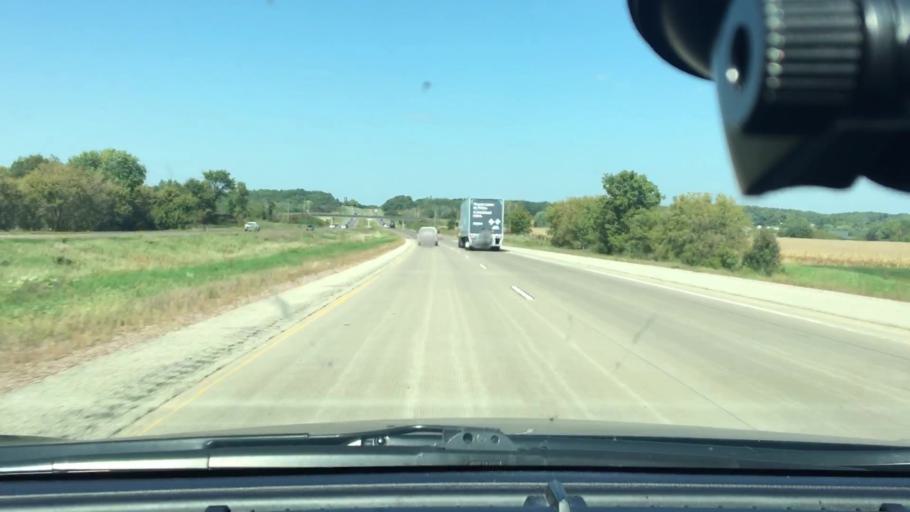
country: US
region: Wisconsin
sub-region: Eau Claire County
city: Eau Claire
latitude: 44.8169
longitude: -91.5647
